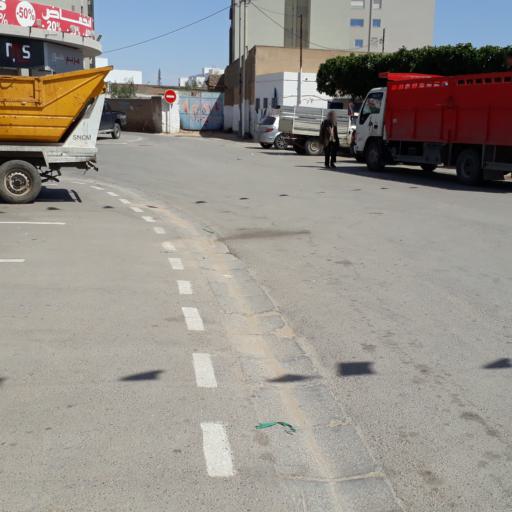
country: TN
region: Safaqis
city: Al Qarmadah
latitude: 34.8035
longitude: 10.7607
